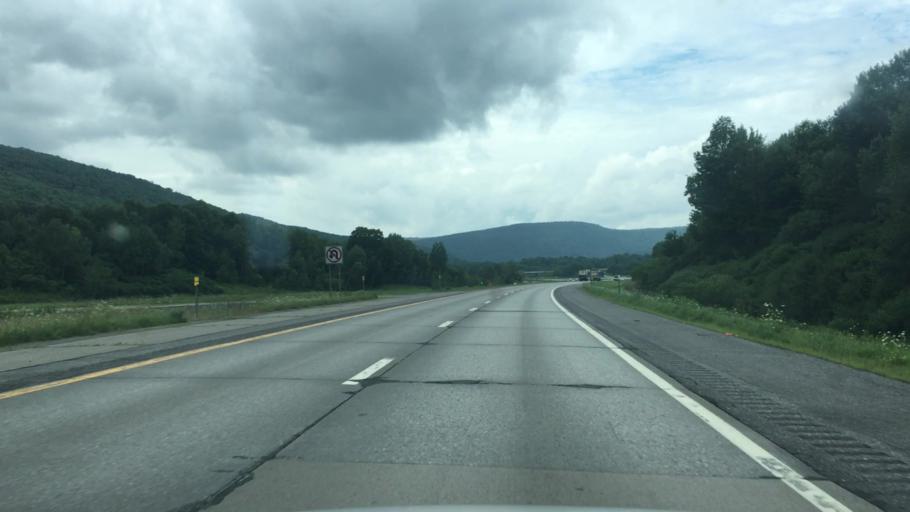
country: US
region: New York
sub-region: Otsego County
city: Worcester
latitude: 42.5953
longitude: -74.7157
